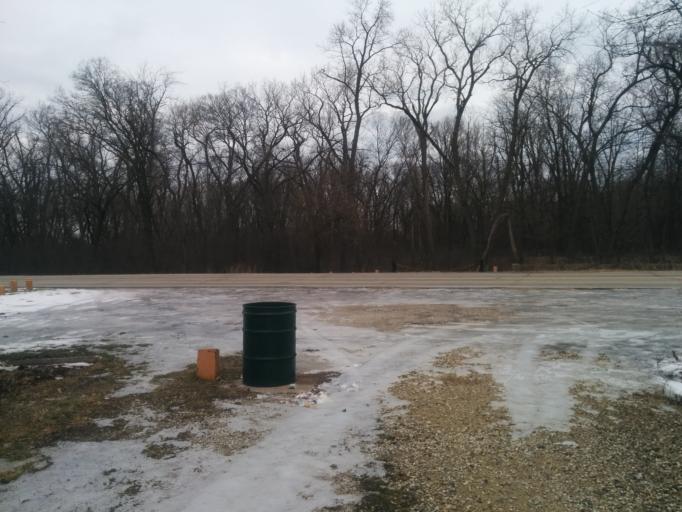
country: US
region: Illinois
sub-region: Cook County
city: Winnetka
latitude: 42.1027
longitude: -87.7581
